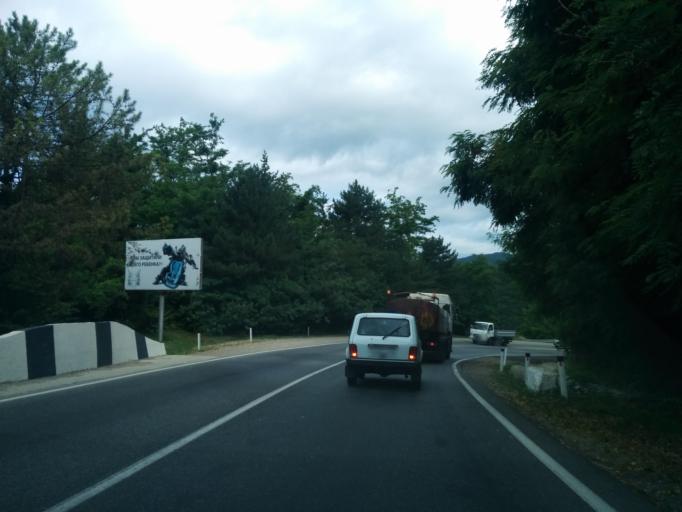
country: RU
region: Krasnodarskiy
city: Agoy
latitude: 44.1395
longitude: 39.0545
